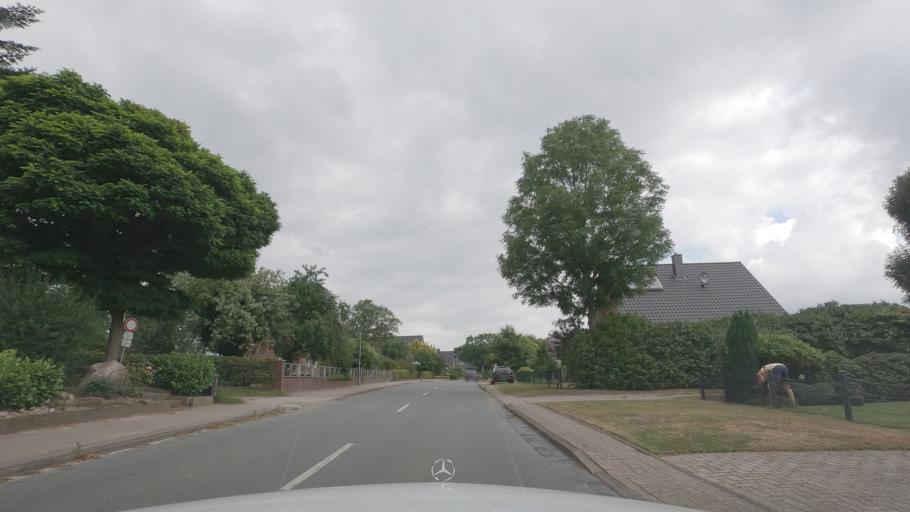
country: DE
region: Lower Saxony
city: Neuenkirchen
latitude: 53.2366
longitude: 8.5275
